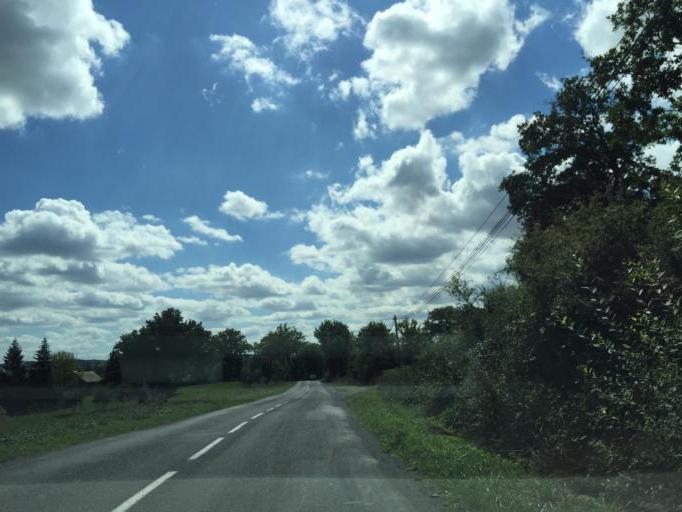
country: FR
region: Midi-Pyrenees
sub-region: Departement de l'Aveyron
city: Pont-de-Salars
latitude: 44.2993
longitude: 2.7306
